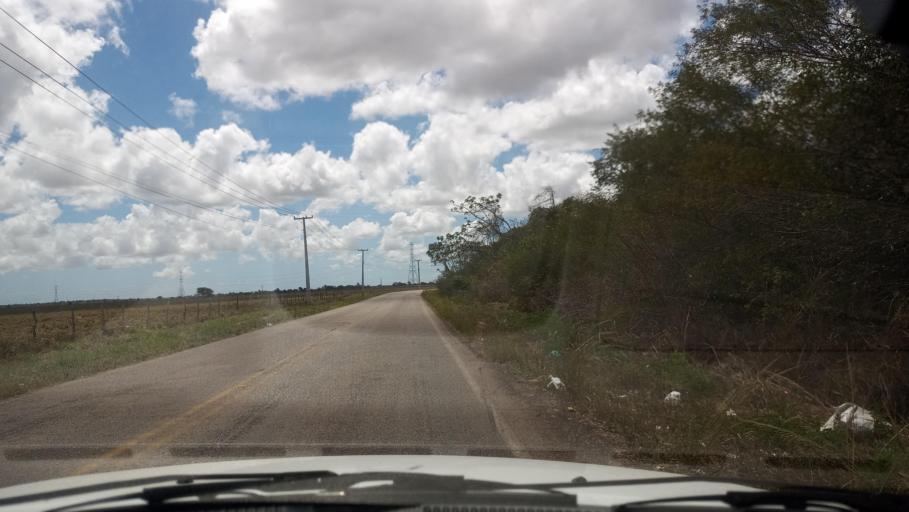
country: BR
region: Rio Grande do Norte
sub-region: Brejinho
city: Brejinho
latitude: -6.0408
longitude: -35.4180
